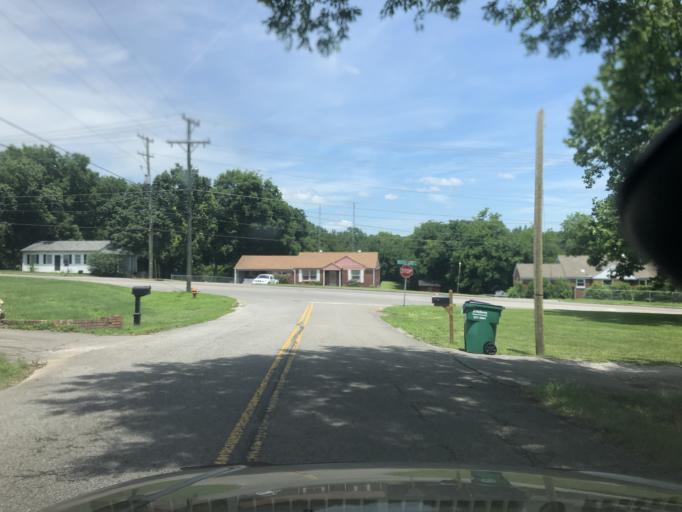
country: US
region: Tennessee
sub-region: Davidson County
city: Lakewood
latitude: 36.2520
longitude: -86.6946
